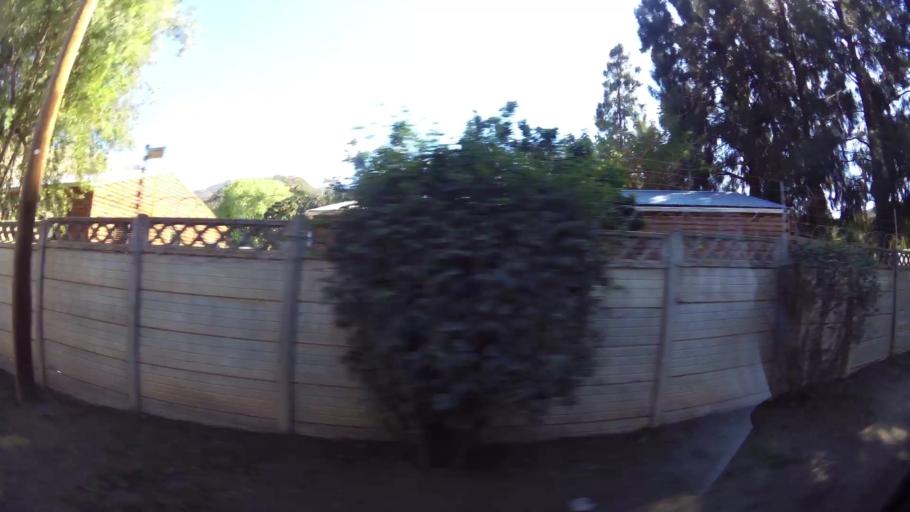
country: ZA
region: Western Cape
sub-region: Cape Winelands District Municipality
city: Ashton
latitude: -33.7869
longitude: 20.1138
